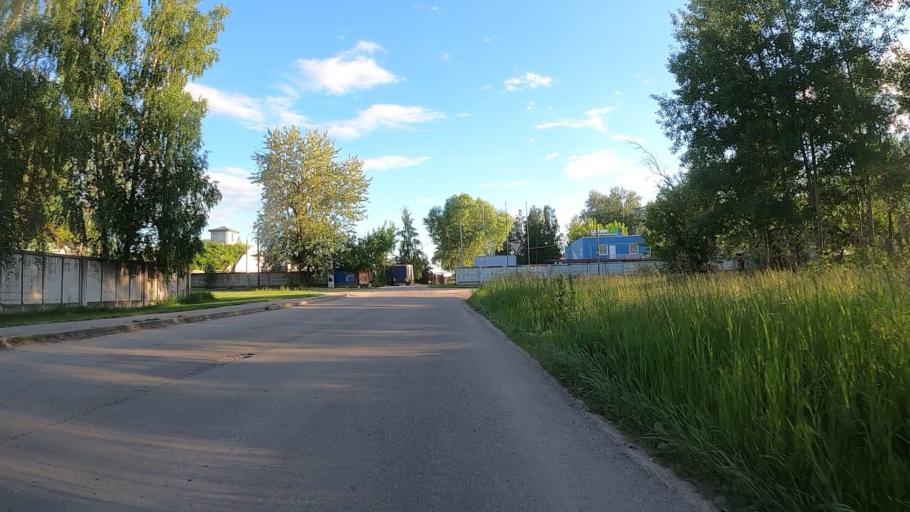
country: LV
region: Kekava
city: Kekava
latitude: 56.8925
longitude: 24.2183
